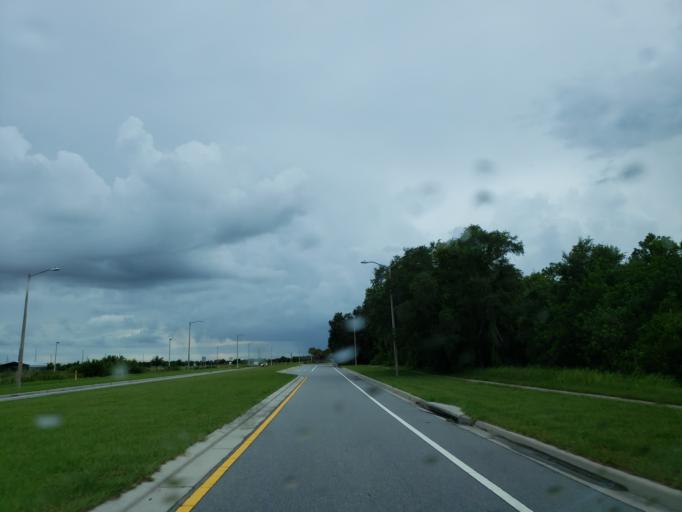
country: US
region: Florida
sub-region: Hillsborough County
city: Sun City Center
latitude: 27.7292
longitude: -82.3917
